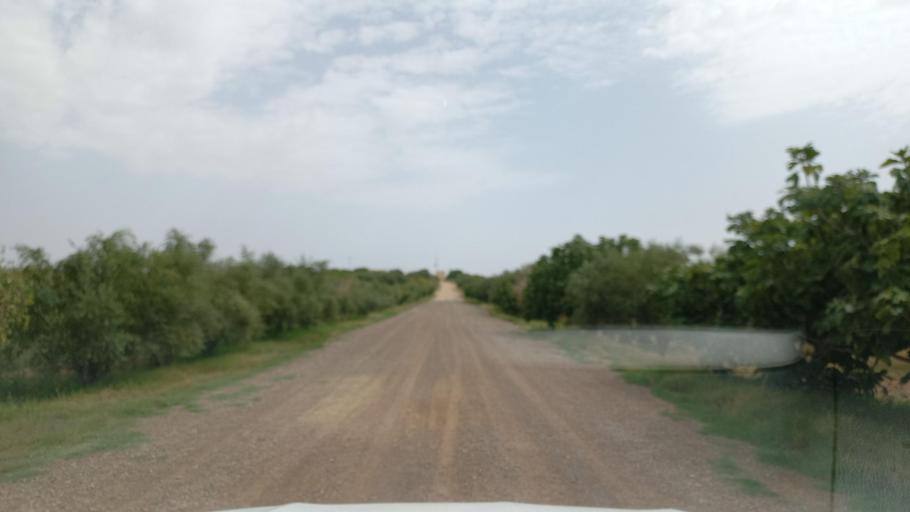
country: TN
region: Al Qasrayn
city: Kasserine
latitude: 35.2708
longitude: 9.0081
